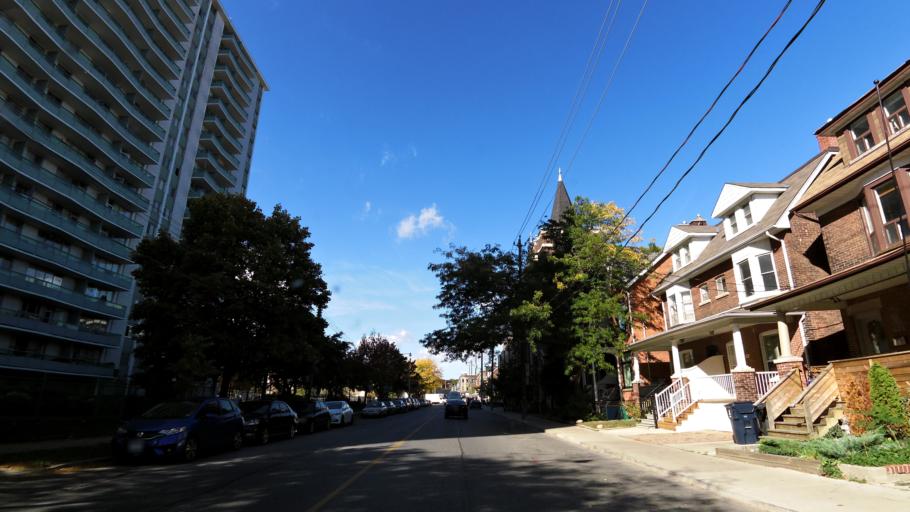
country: CA
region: Ontario
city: Toronto
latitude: 43.6596
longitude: -79.4287
